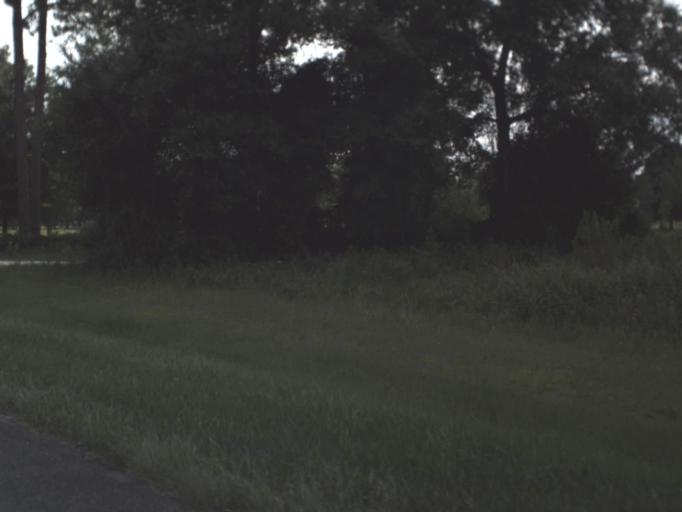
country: US
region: Florida
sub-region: Bradford County
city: Starke
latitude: 30.0300
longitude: -82.1590
